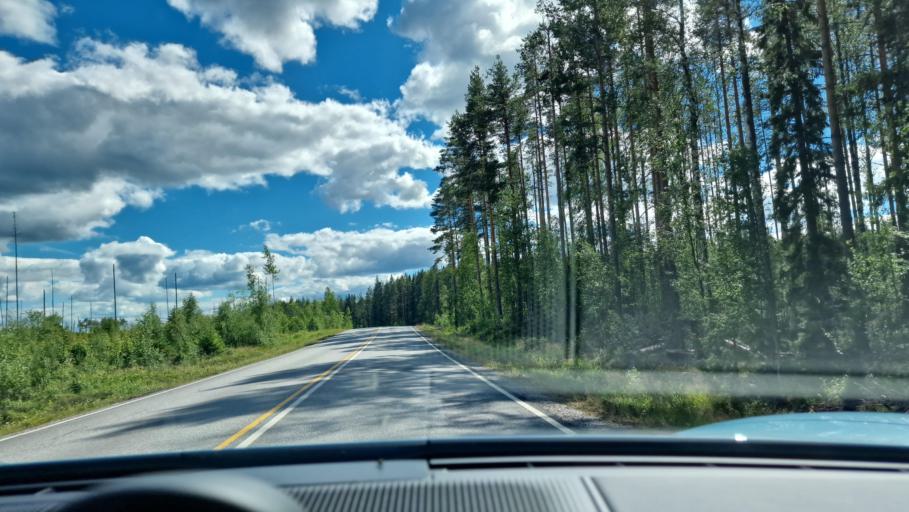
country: FI
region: Central Finland
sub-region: Saarijaervi-Viitasaari
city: Pylkoenmaeki
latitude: 62.6503
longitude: 24.5724
